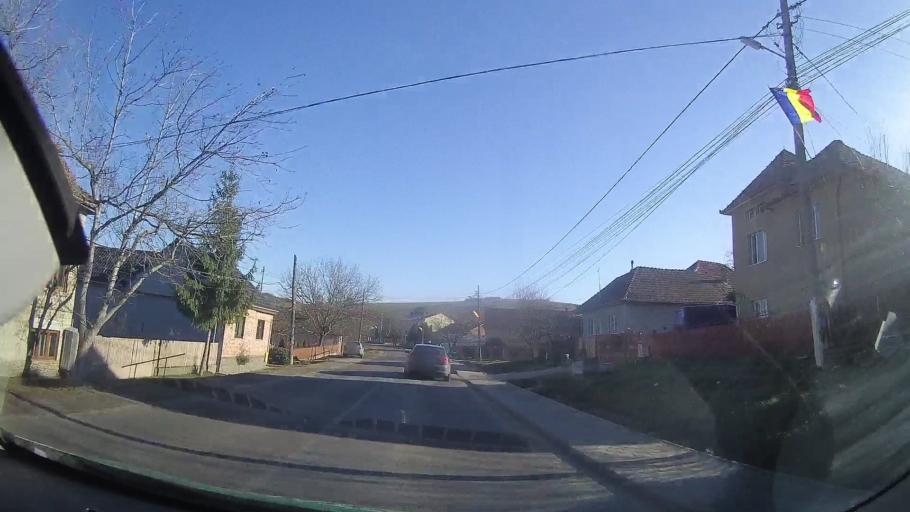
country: RO
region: Mures
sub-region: Comuna Sarmasu
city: Sarmasu
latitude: 46.7580
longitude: 24.1672
